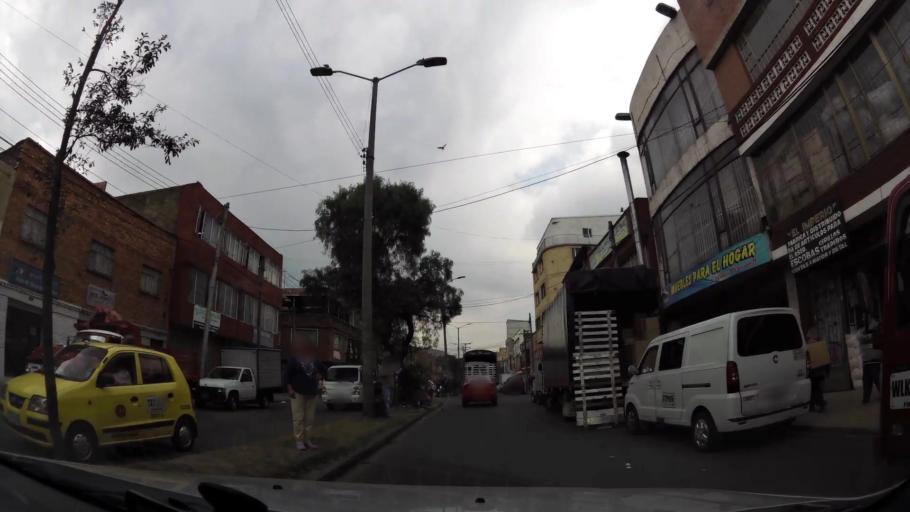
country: CO
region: Bogota D.C.
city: Bogota
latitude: 4.5774
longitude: -74.1246
